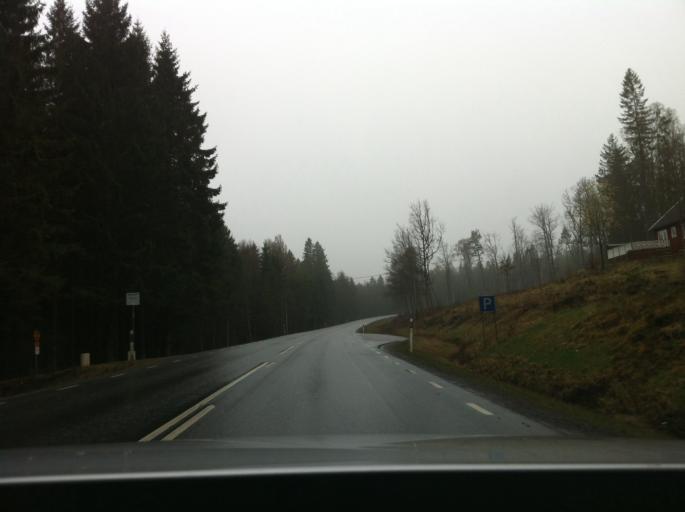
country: SE
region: Vaestra Goetaland
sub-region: Alingsas Kommun
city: Sollebrunn
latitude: 58.0260
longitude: 12.4608
